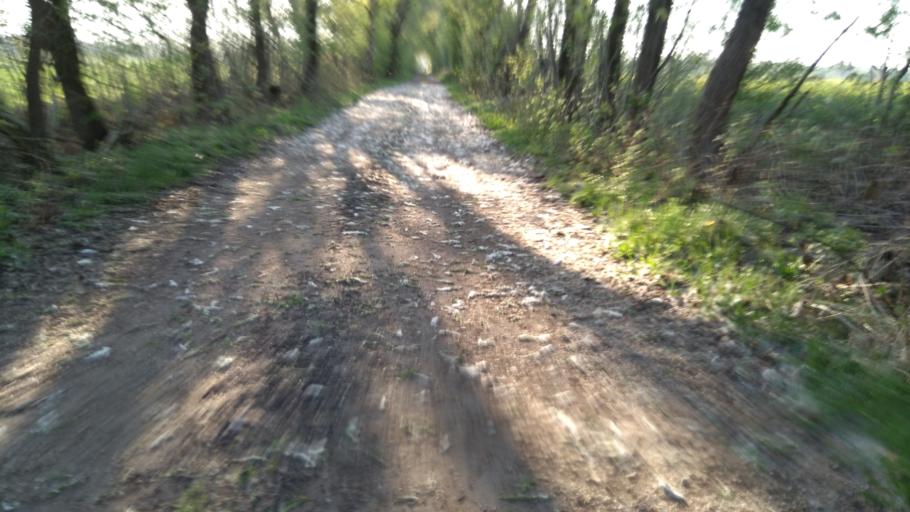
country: DE
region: Lower Saxony
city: Apensen
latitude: 53.4377
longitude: 9.5770
